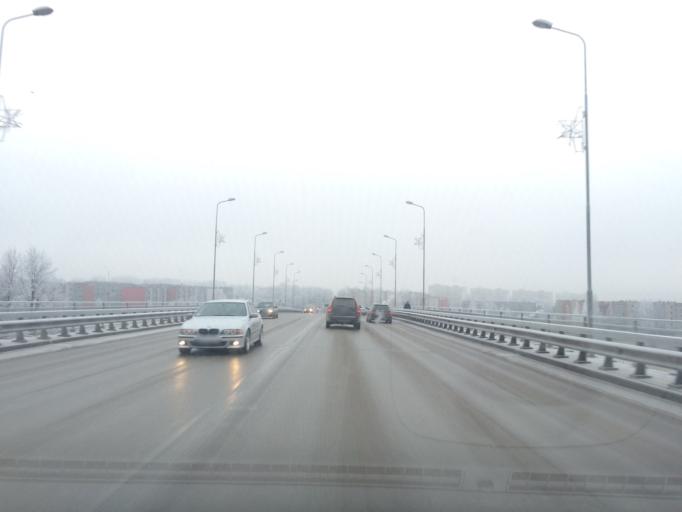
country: LV
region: Rezekne
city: Rezekne
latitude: 56.5211
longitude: 27.3396
